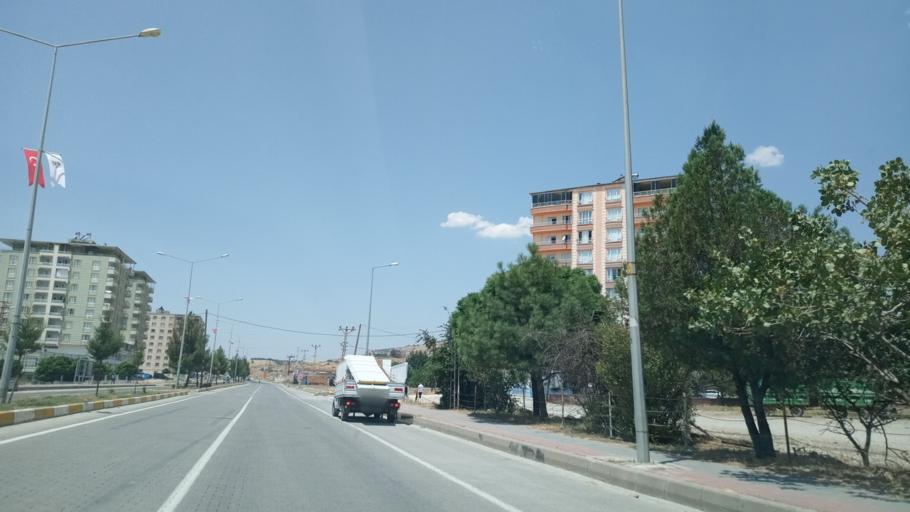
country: TR
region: Batman
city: Kozluk
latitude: 38.1677
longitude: 41.4924
